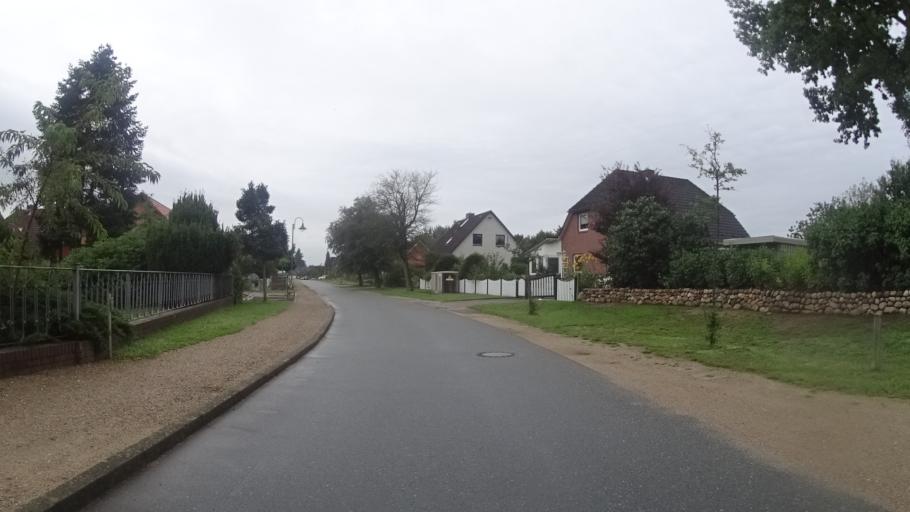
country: DE
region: Schleswig-Holstein
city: Siebeneichen
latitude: 53.5088
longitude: 10.6153
